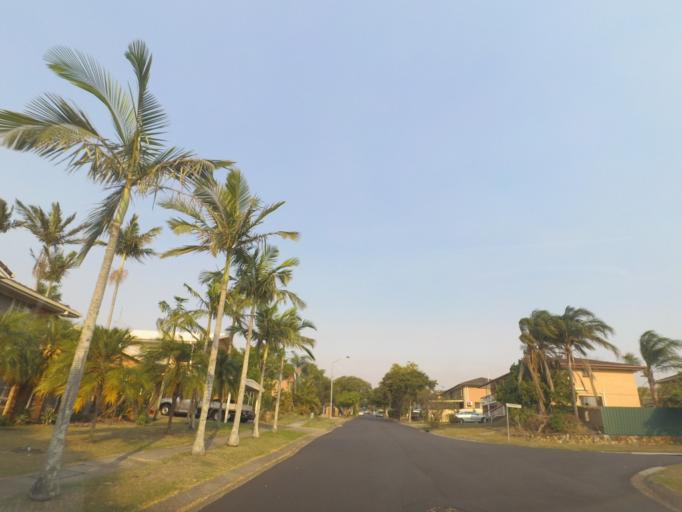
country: AU
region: Queensland
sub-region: Brisbane
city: Nathan
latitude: -27.5605
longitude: 153.0575
